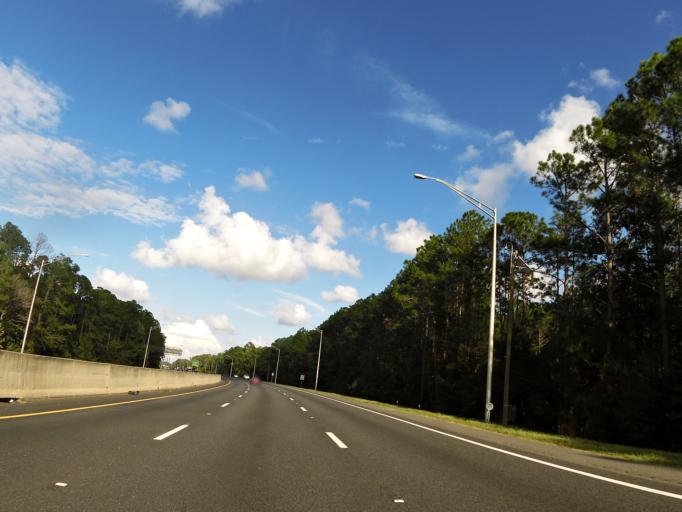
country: US
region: Florida
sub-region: Saint Johns County
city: Ponte Vedra Beach
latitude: 30.2526
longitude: -81.4540
